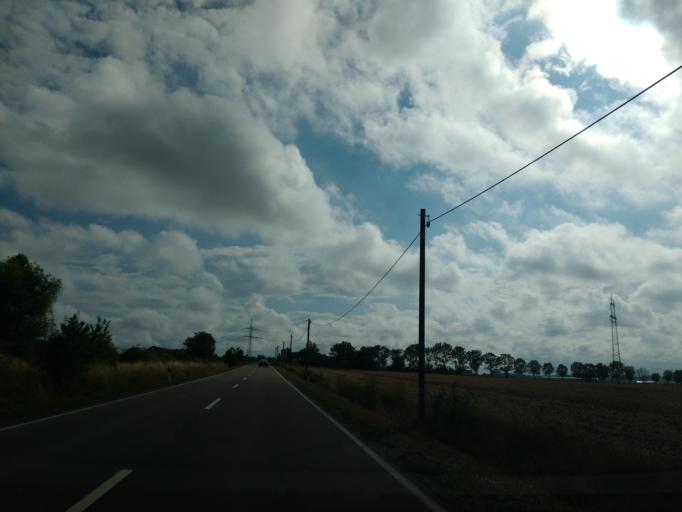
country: DE
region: Saxony-Anhalt
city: Niemberg
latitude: 51.5590
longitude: 12.1233
